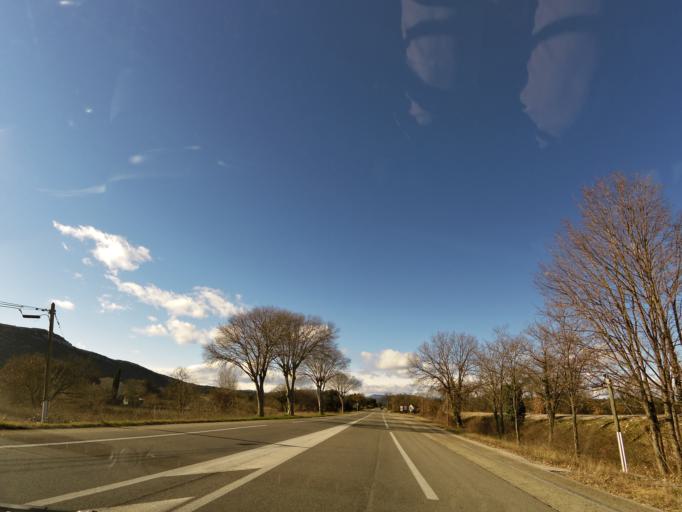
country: FR
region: Languedoc-Roussillon
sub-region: Departement du Gard
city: Sauve
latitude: 43.9339
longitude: 3.9754
